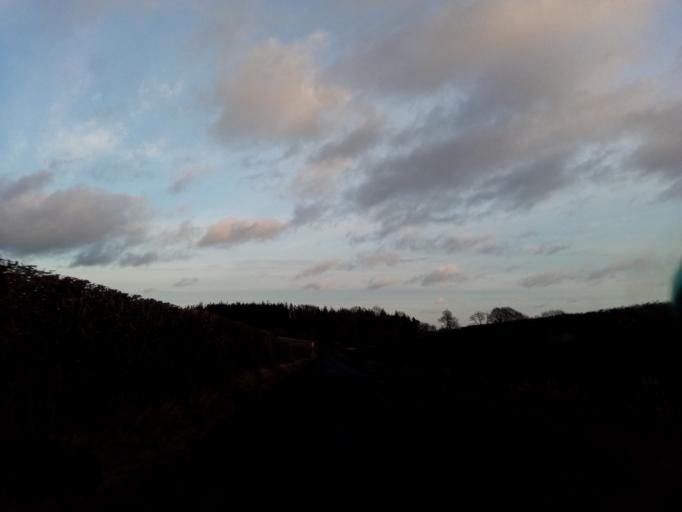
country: GB
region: Scotland
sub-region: The Scottish Borders
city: Newtown St Boswells
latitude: 55.5492
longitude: -2.6975
